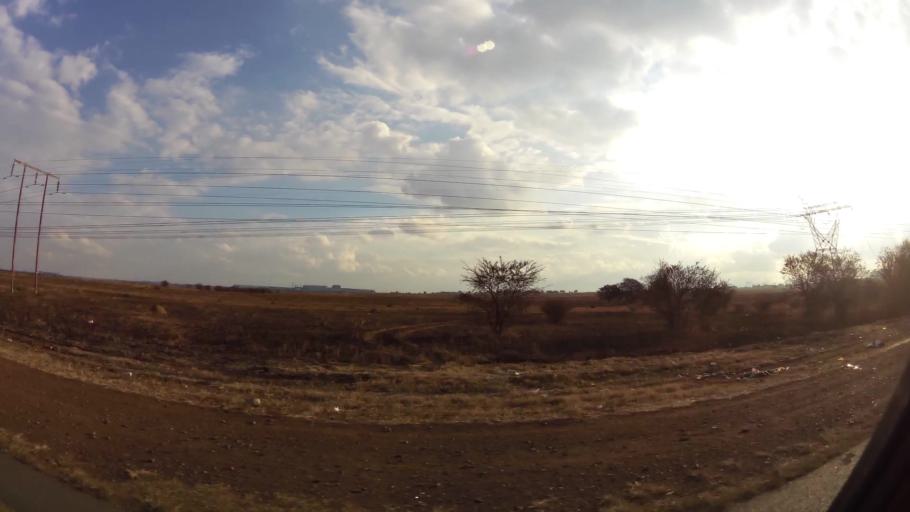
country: ZA
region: Gauteng
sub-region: Sedibeng District Municipality
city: Vereeniging
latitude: -26.6282
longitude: 27.8664
